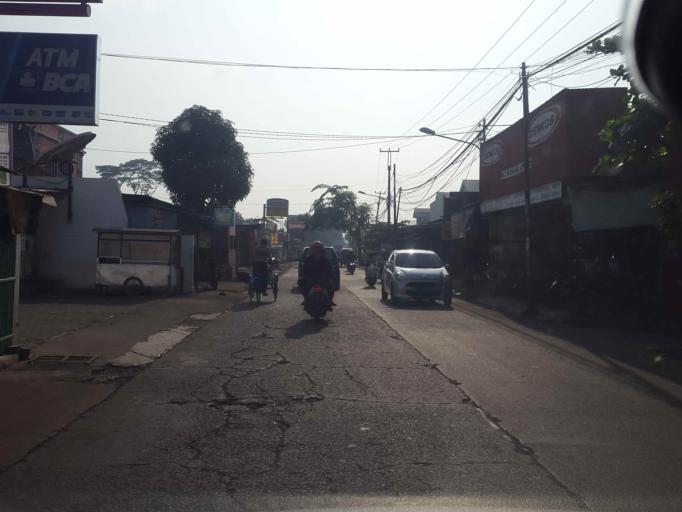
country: ID
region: West Java
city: Bekasi
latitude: -6.3146
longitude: 106.9967
